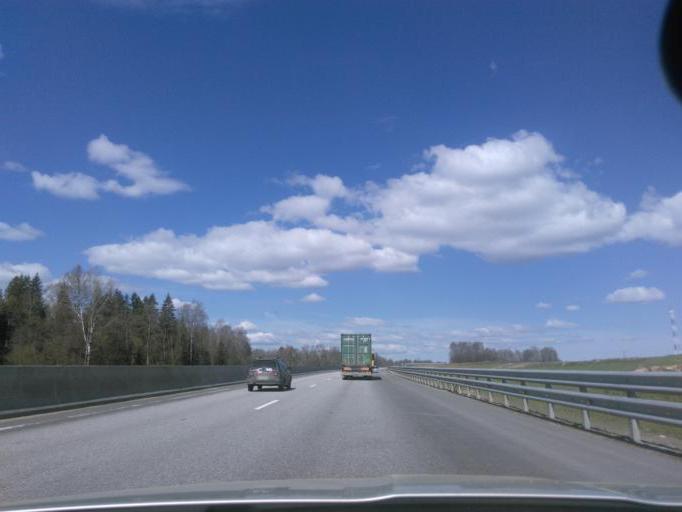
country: RU
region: Moskovskaya
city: Lozhki
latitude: 56.1051
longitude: 37.1379
